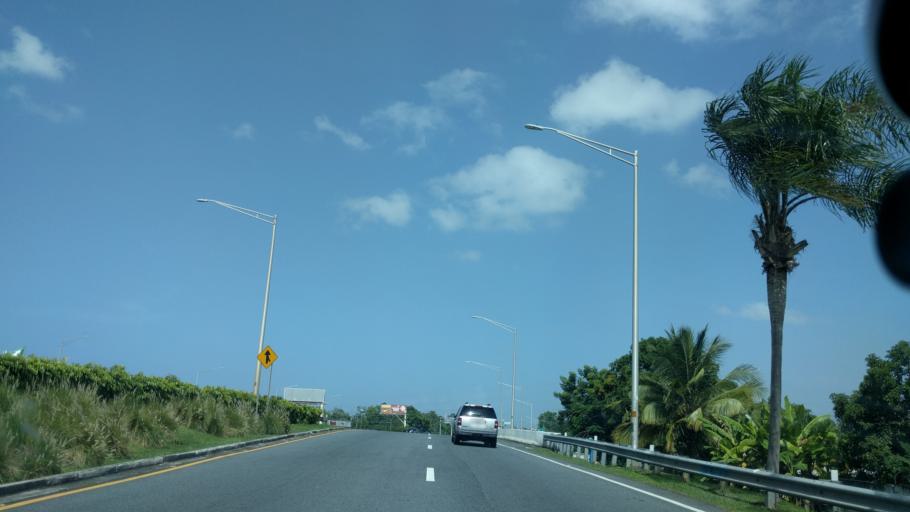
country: PR
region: Toa Baja
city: Sabana Seca
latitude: 18.4206
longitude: -66.1629
